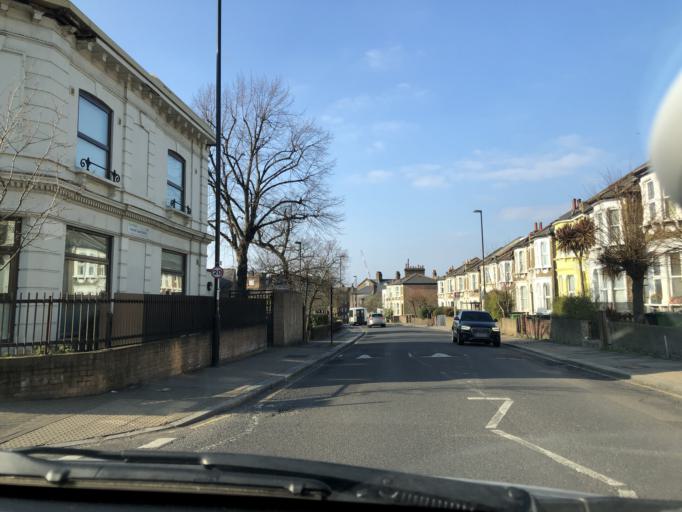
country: GB
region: England
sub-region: Greater London
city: Catford
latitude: 51.4538
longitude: -0.0084
